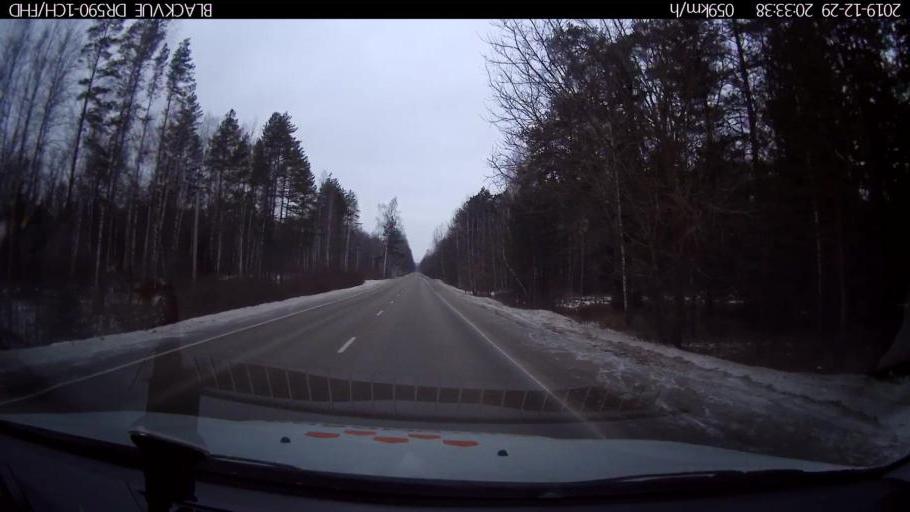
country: RU
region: Nizjnij Novgorod
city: Afonino
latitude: 56.1816
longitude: 44.0495
